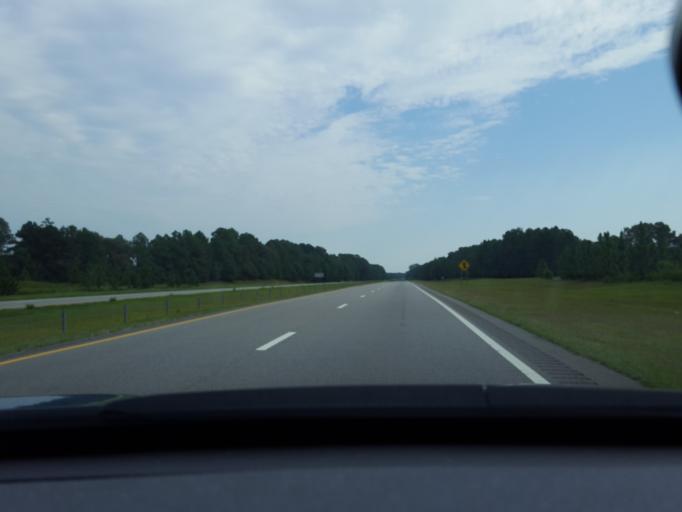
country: US
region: North Carolina
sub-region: Chowan County
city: Edenton
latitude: 36.0596
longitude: -76.6680
